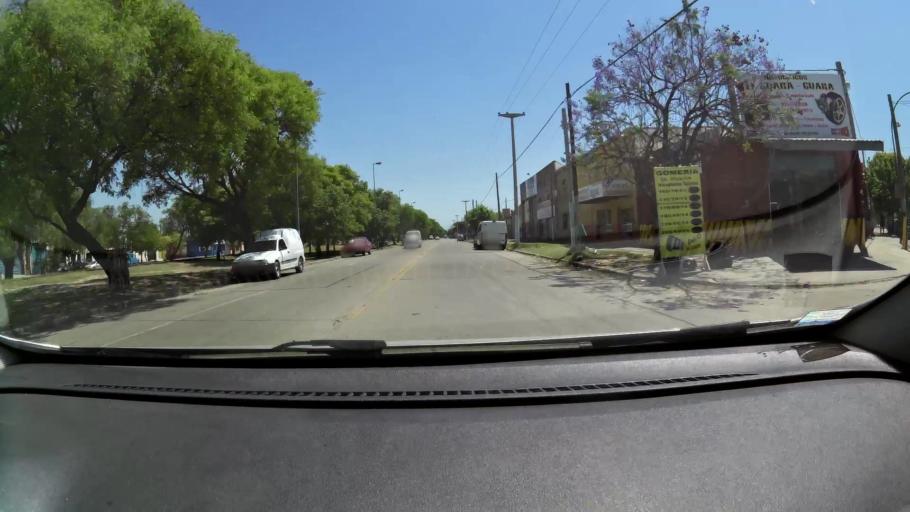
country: AR
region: Cordoba
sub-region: Departamento de Capital
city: Cordoba
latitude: -31.3931
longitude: -64.1516
